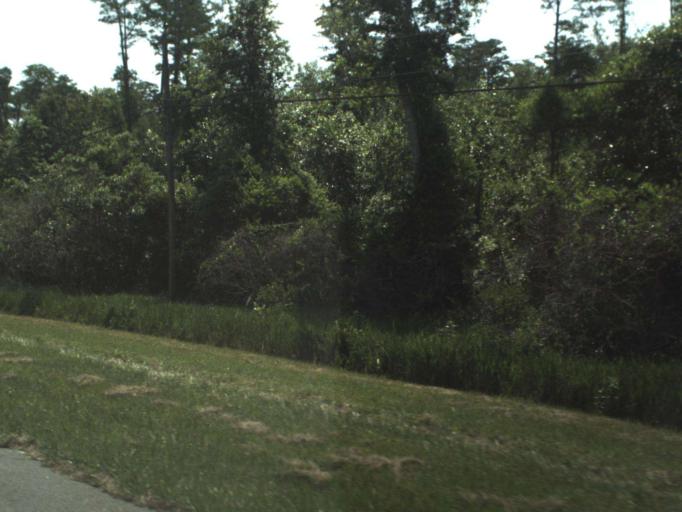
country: US
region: Florida
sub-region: Volusia County
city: Samsula-Spruce Creek
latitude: 29.1260
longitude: -81.1657
